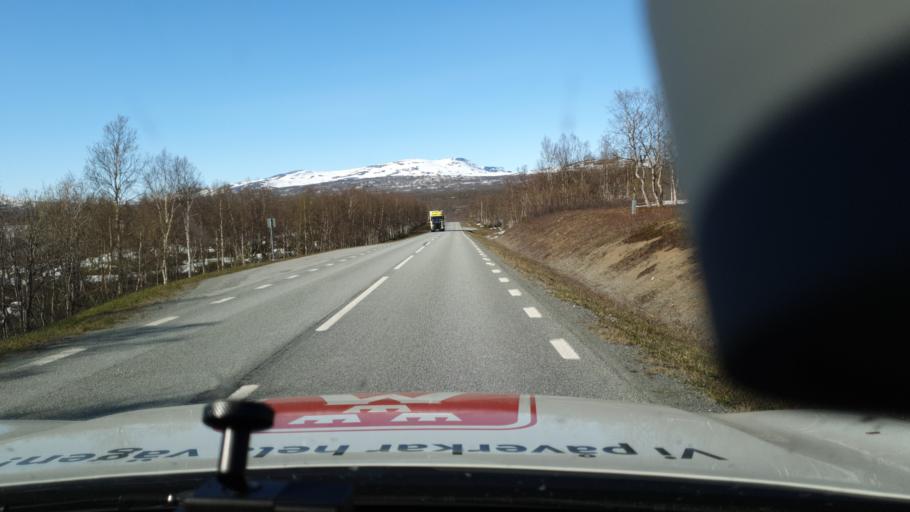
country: NO
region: Nordland
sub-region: Rana
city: Mo i Rana
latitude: 66.0042
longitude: 15.0927
